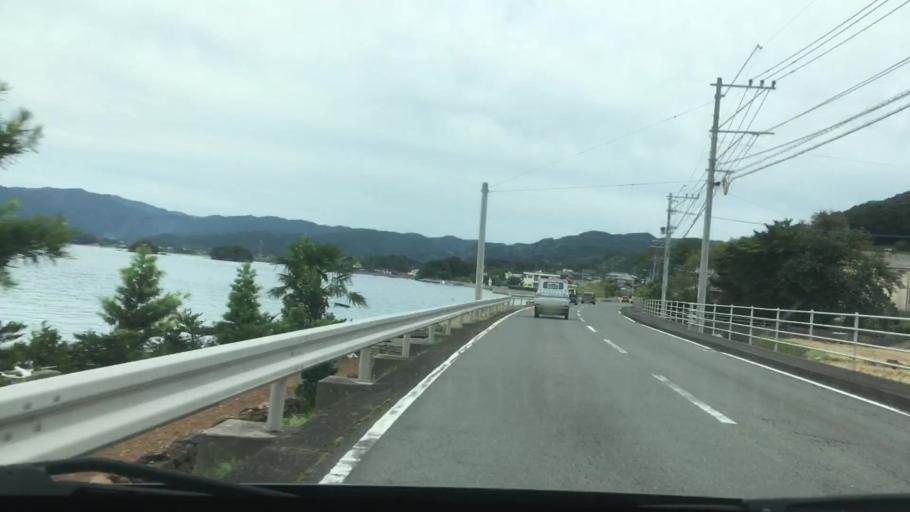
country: JP
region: Nagasaki
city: Sasebo
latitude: 33.0246
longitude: 129.7392
